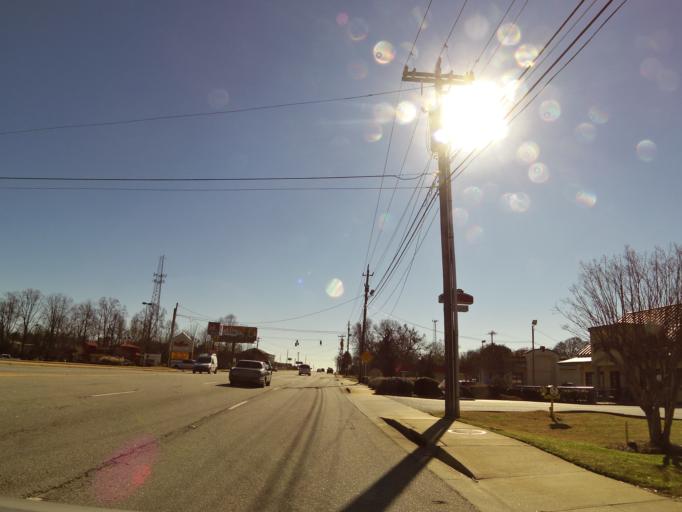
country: US
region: South Carolina
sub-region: Greenville County
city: Sans Souci
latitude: 34.8886
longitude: -82.4056
